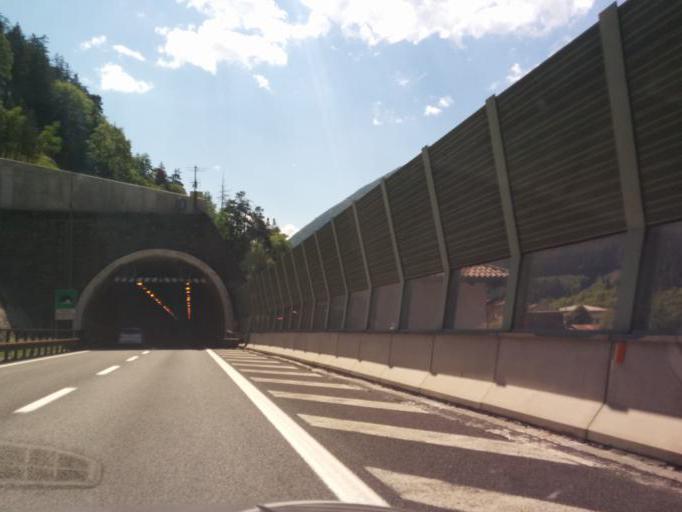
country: IT
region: Trentino-Alto Adige
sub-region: Bolzano
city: Fortezza
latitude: 46.7927
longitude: 11.6098
